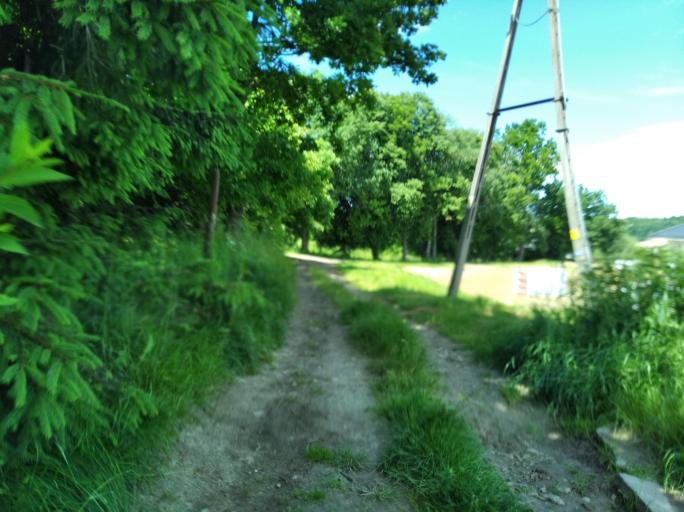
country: PL
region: Subcarpathian Voivodeship
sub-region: Powiat strzyzowski
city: Strzyzow
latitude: 49.8440
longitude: 21.8051
